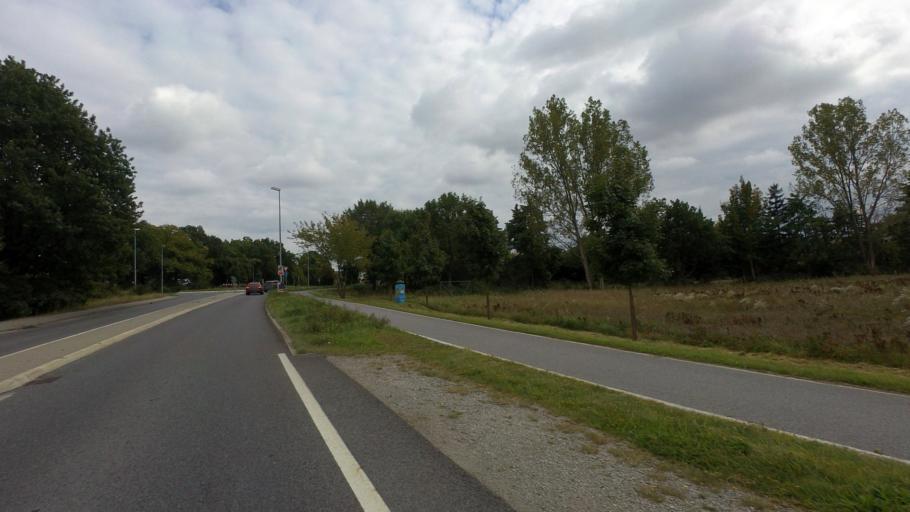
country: DE
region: Saxony
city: Hoyerswerda
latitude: 51.4456
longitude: 14.2415
